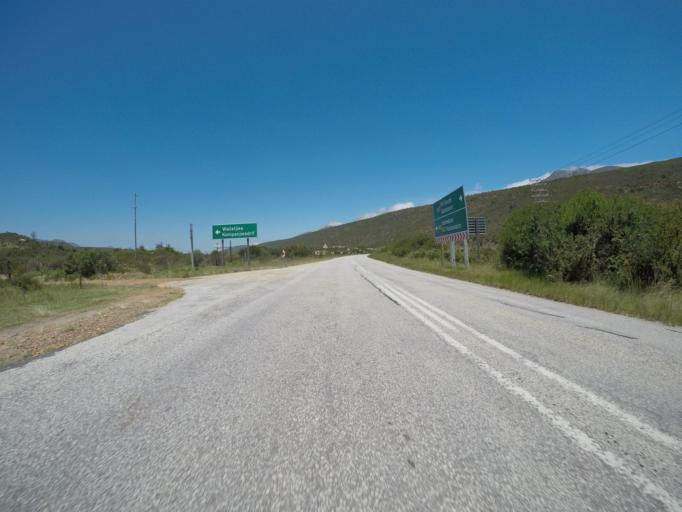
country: ZA
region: Eastern Cape
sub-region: Cacadu District Municipality
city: Kareedouw
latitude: -33.8761
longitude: 24.0515
